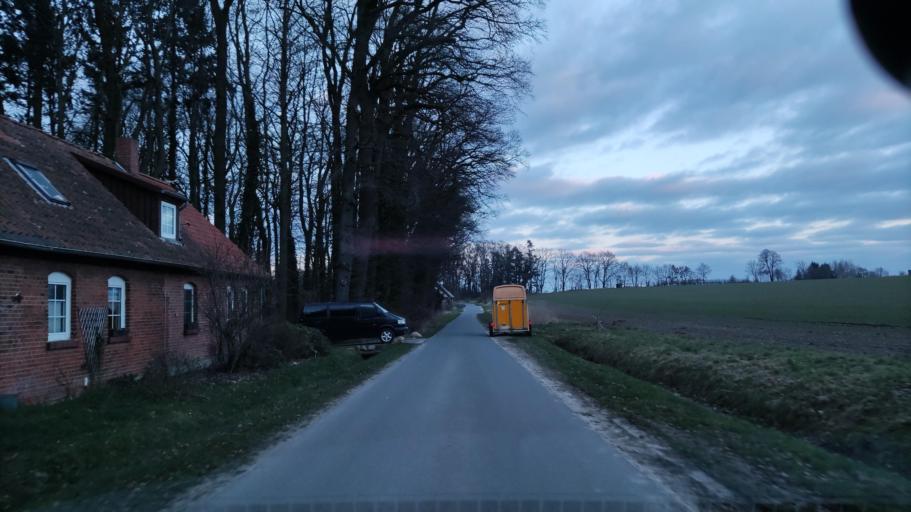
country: DE
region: Lower Saxony
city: Ebstorf
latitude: 53.0723
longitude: 10.4241
